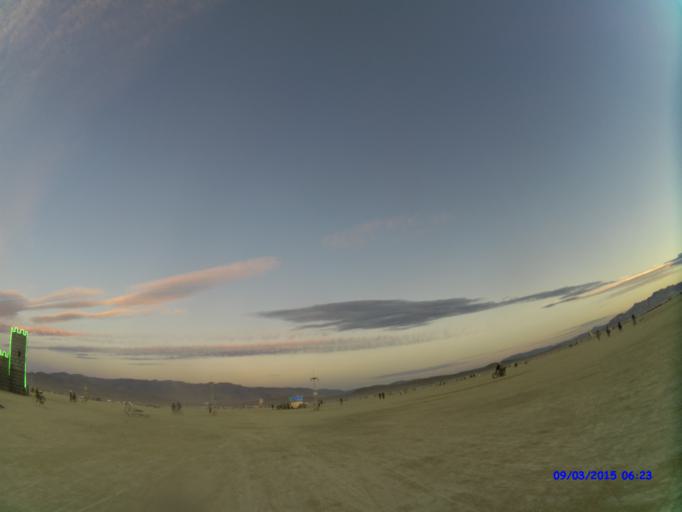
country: US
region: Nevada
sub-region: Pershing County
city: Lovelock
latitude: 40.7844
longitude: -119.1970
